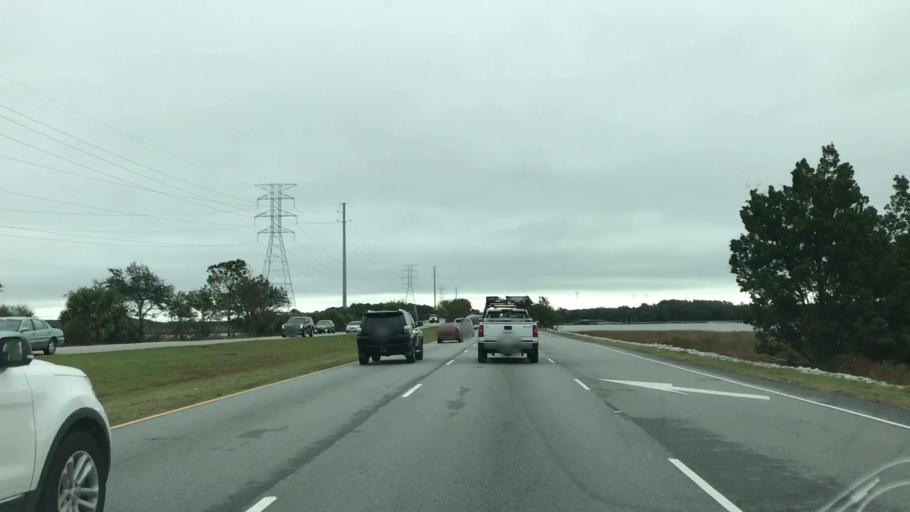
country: US
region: South Carolina
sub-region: Beaufort County
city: Hilton Head Island
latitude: 32.2320
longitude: -80.7961
